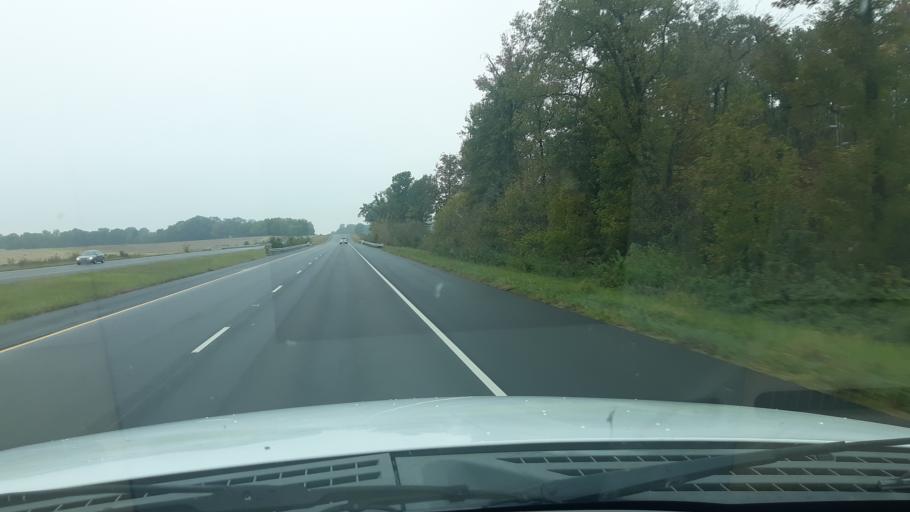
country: US
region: Illinois
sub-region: Saline County
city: Eldorado
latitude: 37.7974
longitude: -88.4672
